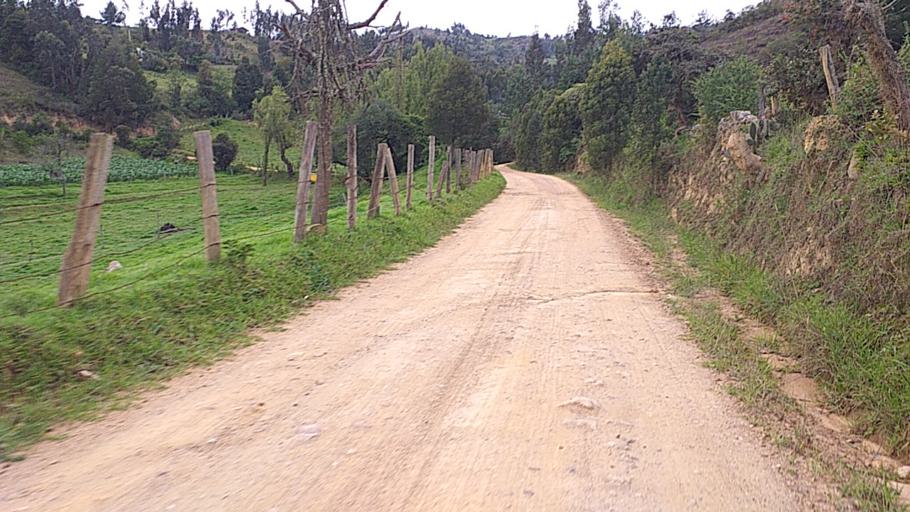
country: CO
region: Boyaca
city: Floresta
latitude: 5.8739
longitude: -72.9176
